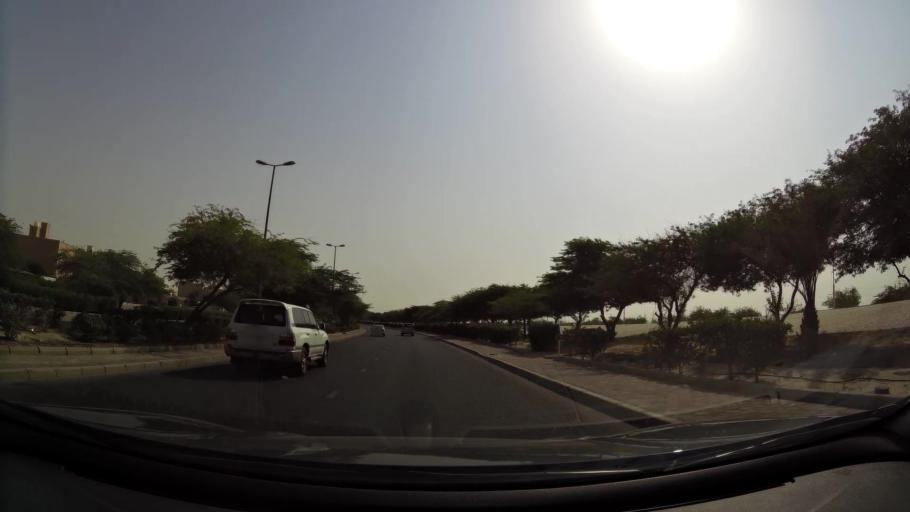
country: KW
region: Muhafazat al Jahra'
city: Al Jahra'
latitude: 29.3281
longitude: 47.6471
